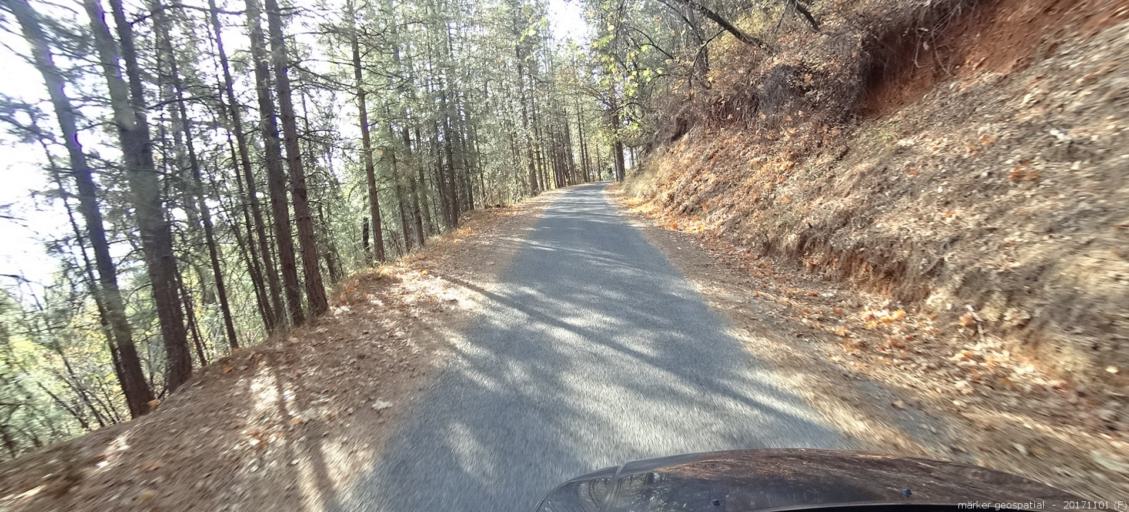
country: US
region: California
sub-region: Shasta County
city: Shasta Lake
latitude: 40.8115
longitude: -122.3107
